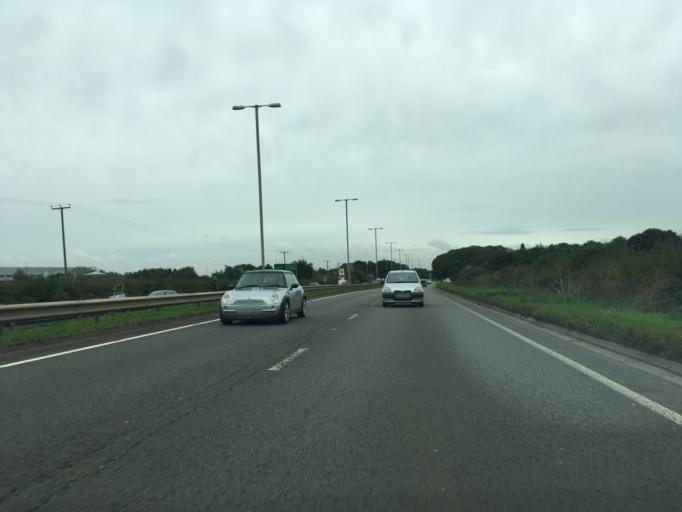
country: GB
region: England
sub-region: Nottinghamshire
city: South Collingham
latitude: 53.0973
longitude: -0.7807
